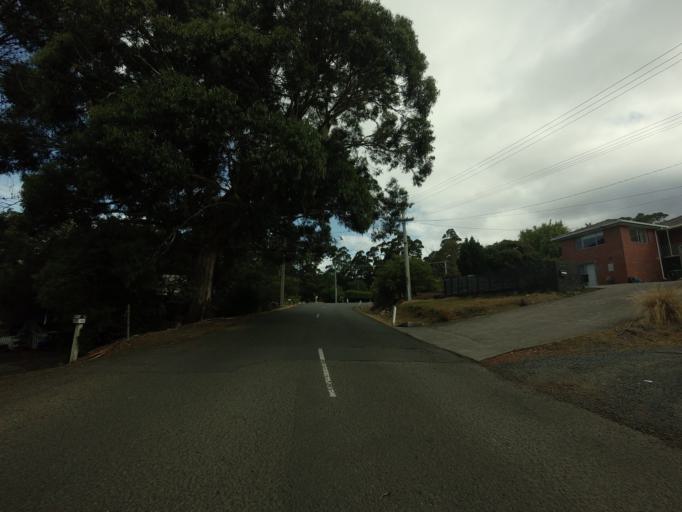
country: AU
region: Tasmania
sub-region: Hobart
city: Dynnyrne
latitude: -42.9030
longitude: 147.2708
